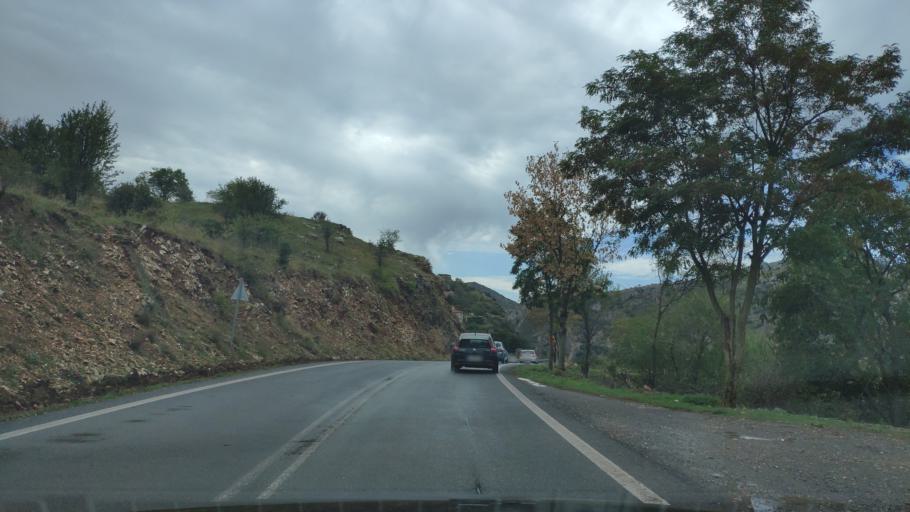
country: GR
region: Peloponnese
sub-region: Nomos Arkadias
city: Dimitsana
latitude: 37.6021
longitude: 22.0396
